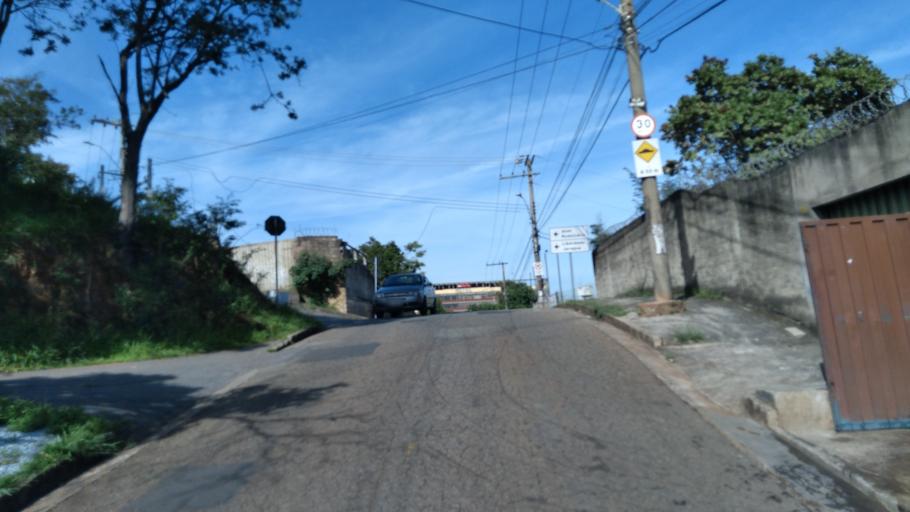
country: BR
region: Minas Gerais
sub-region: Belo Horizonte
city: Belo Horizonte
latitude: -19.8696
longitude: -43.9469
